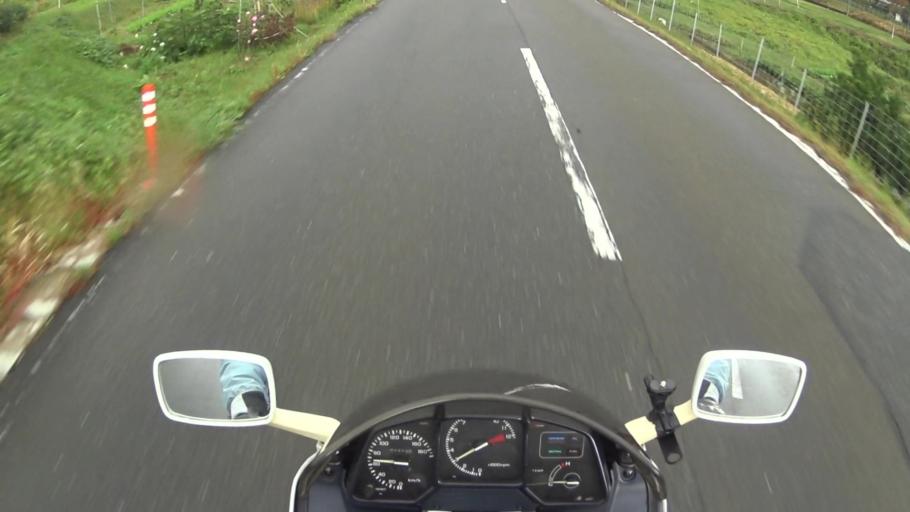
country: JP
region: Kyoto
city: Fukuchiyama
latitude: 35.4115
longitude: 135.1520
